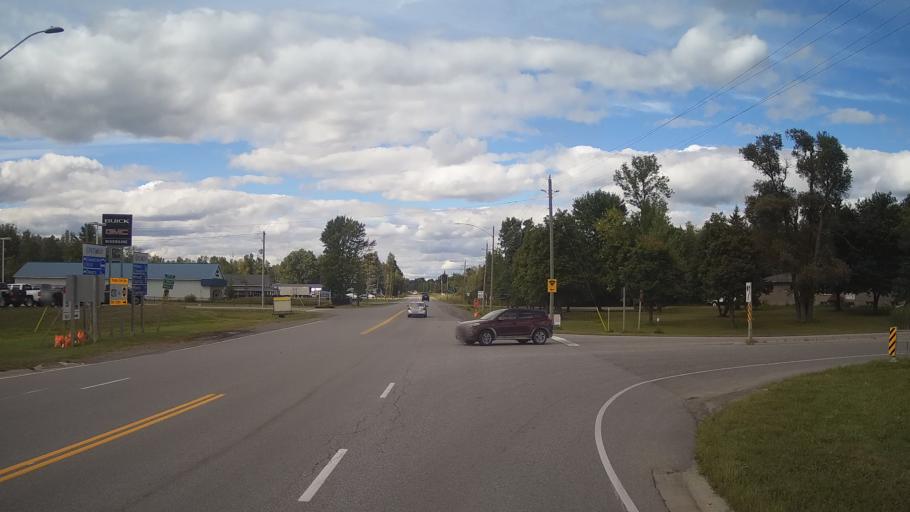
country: CA
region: Ontario
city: Prescott
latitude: 44.7249
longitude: -75.5263
